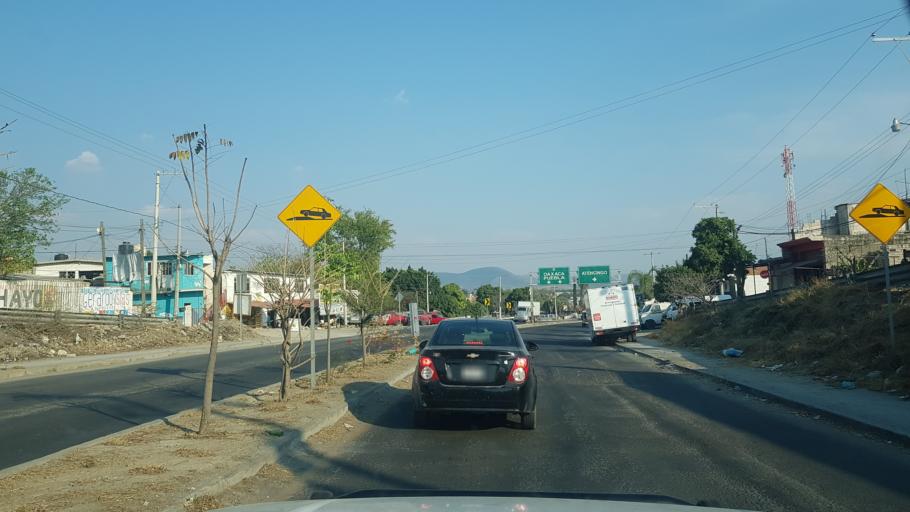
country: MX
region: Puebla
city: Izucar de Matamoros
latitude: 18.6030
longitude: -98.4825
